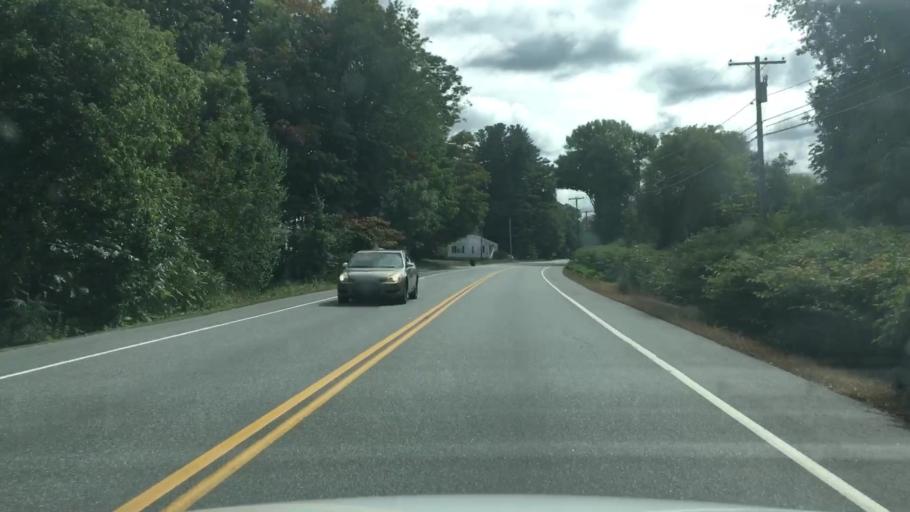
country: US
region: Maine
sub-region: Androscoggin County
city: Lewiston
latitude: 44.0755
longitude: -70.2096
